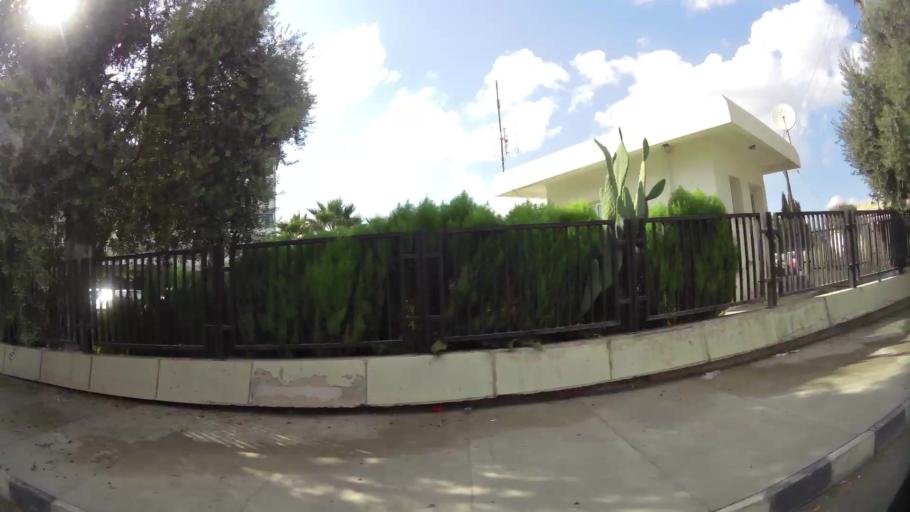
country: CY
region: Lefkosia
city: Nicosia
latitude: 35.1954
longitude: 33.3535
